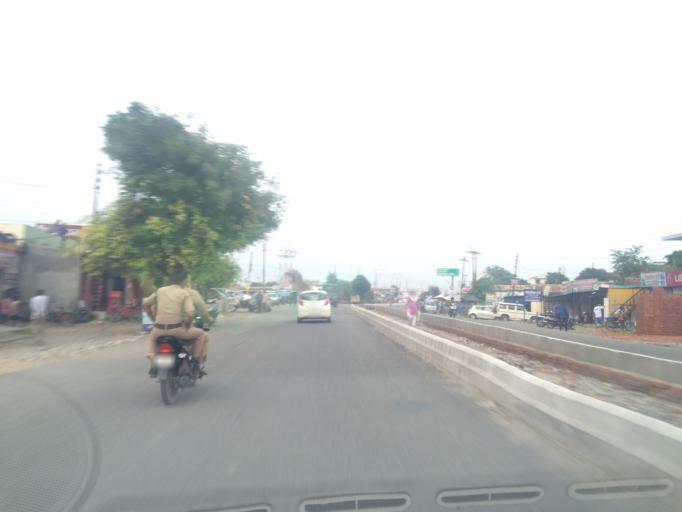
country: IN
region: Uttarakhand
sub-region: Dehradun
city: Doiwala
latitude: 30.1873
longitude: 78.1534
